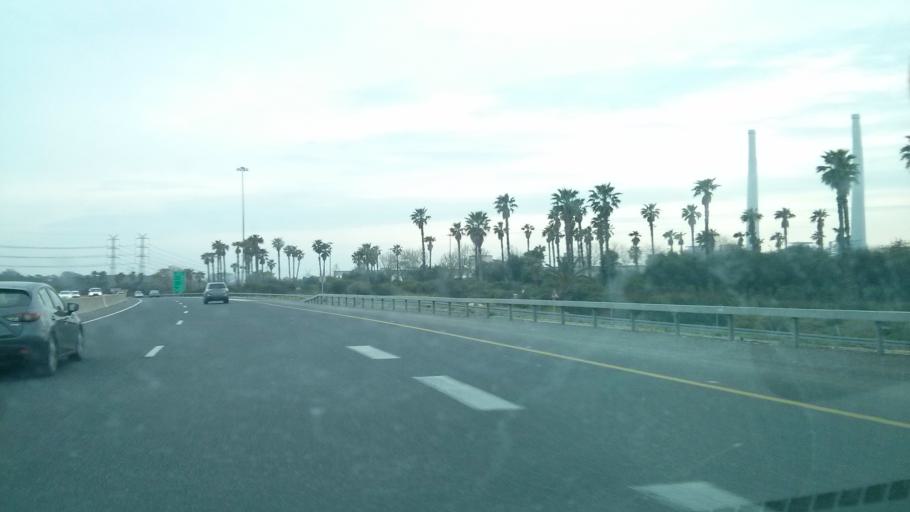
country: IL
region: Haifa
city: Hadera
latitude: 32.4720
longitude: 34.8996
